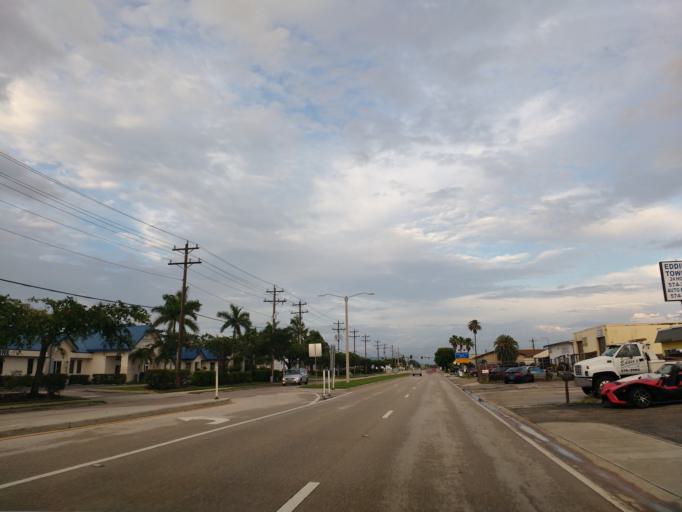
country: US
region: Florida
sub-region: Lee County
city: Lochmoor Waterway Estates
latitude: 26.6361
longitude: -81.9482
